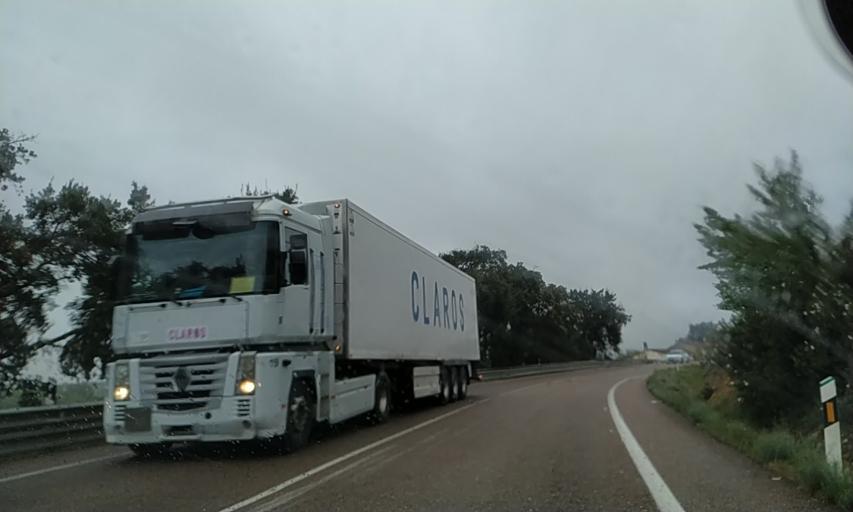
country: ES
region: Extremadura
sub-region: Provincia de Badajoz
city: Puebla de Obando
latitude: 39.1851
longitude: -6.6006
